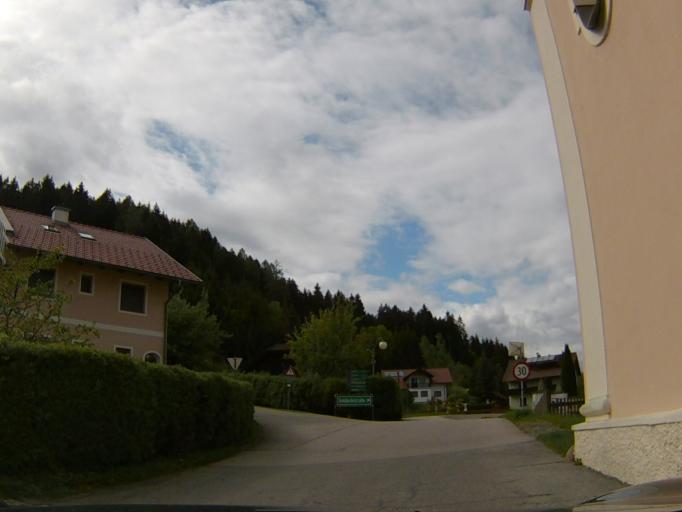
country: AT
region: Carinthia
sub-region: Politischer Bezirk Villach Land
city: Stockenboi
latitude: 46.7292
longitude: 13.5804
